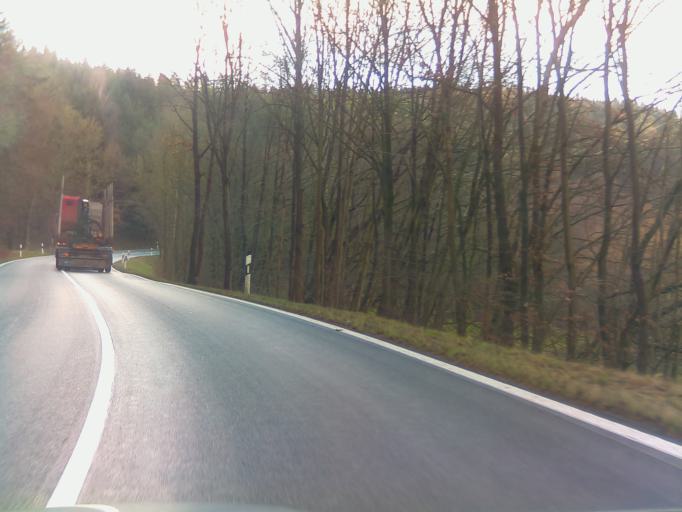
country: DE
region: Thuringia
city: Rosa
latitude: 50.7220
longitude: 10.2861
